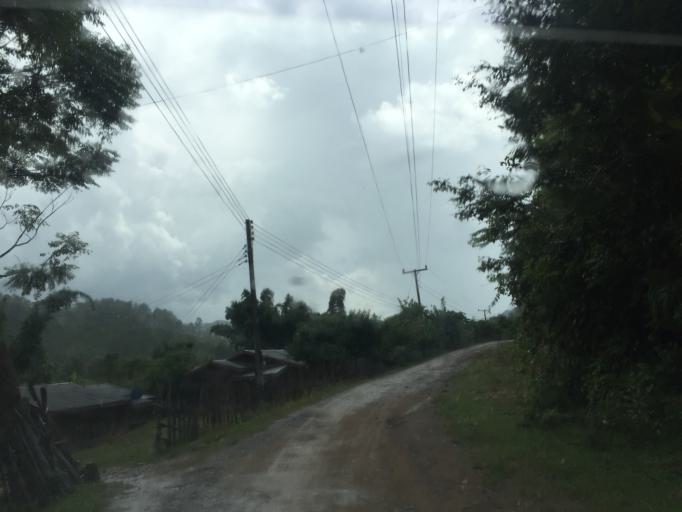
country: LA
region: Xiangkhoang
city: Muang Phonsavan
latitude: 19.3391
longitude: 103.5740
